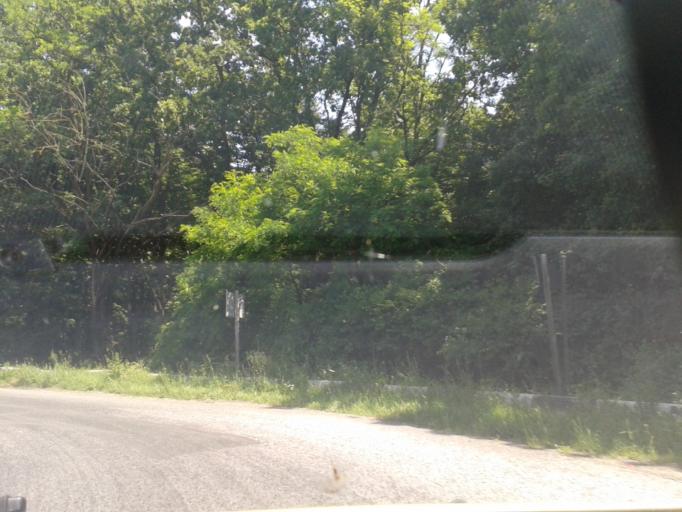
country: RO
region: Hunedoara
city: Lapugiu de Jos
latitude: 45.8851
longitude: 22.4428
